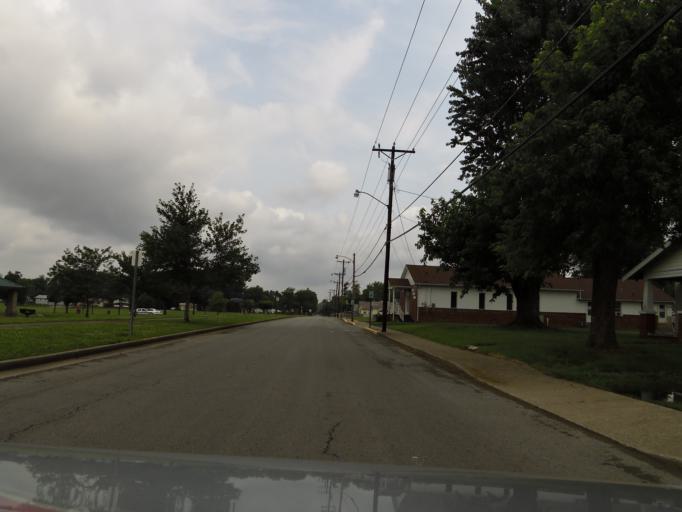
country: US
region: Kentucky
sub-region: Hopkins County
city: Madisonville
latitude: 37.3361
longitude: -87.5023
